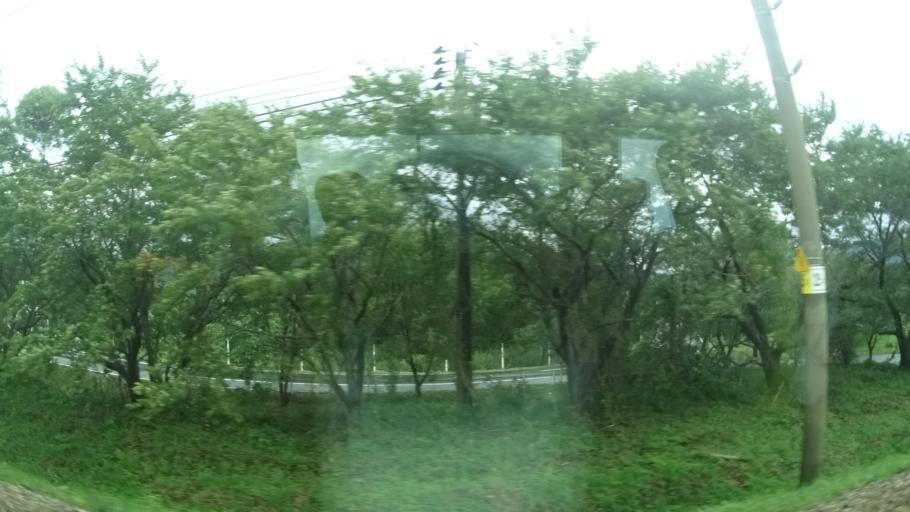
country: JP
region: Niigata
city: Murakami
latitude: 38.1369
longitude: 139.4573
